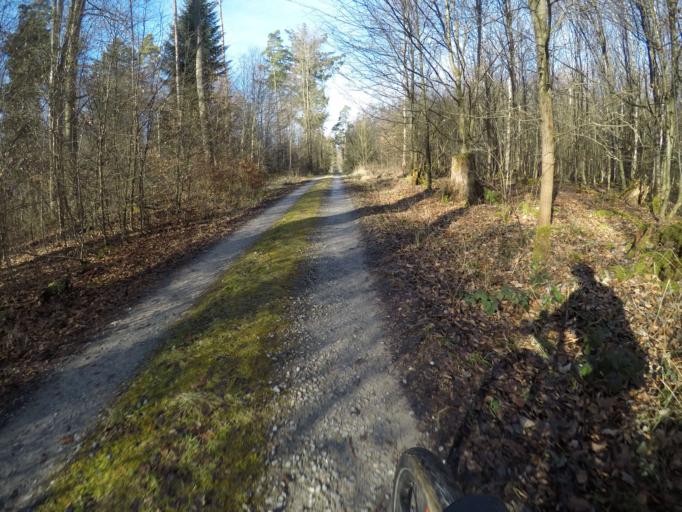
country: DE
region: Baden-Wuerttemberg
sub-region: Regierungsbezirk Stuttgart
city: Steinenbronn
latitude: 48.6878
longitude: 9.0892
